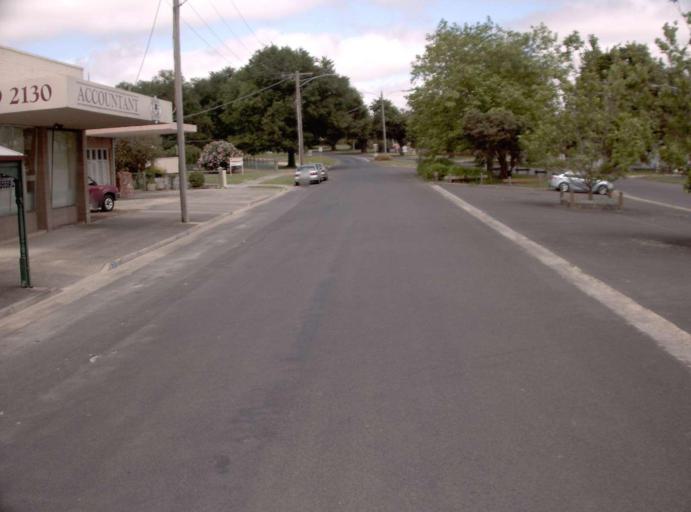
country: AU
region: Victoria
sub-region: Baw Baw
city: Warragul
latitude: -38.3427
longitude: 145.7633
